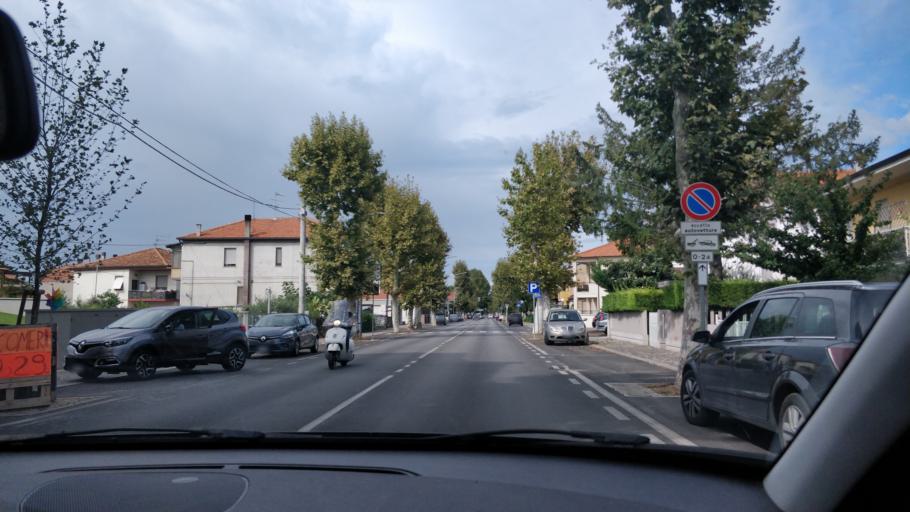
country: IT
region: Abruzzo
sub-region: Provincia di Chieti
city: Sambuceto
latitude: 42.4212
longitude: 14.1824
